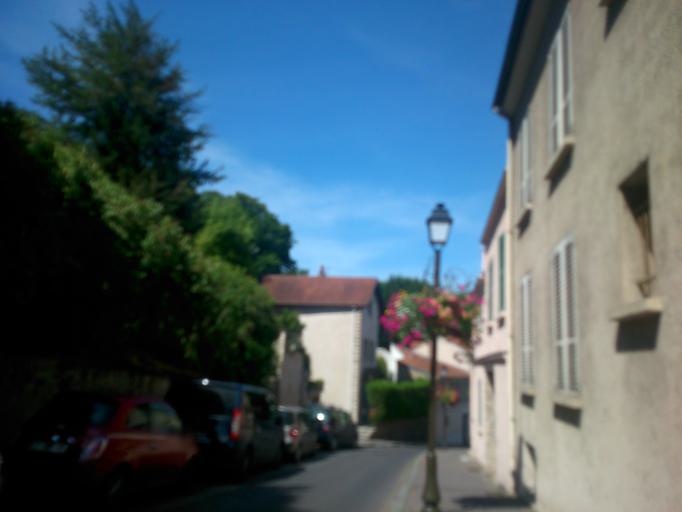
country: FR
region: Ile-de-France
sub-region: Departement des Yvelines
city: Le Pecq
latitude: 48.8961
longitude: 2.1028
